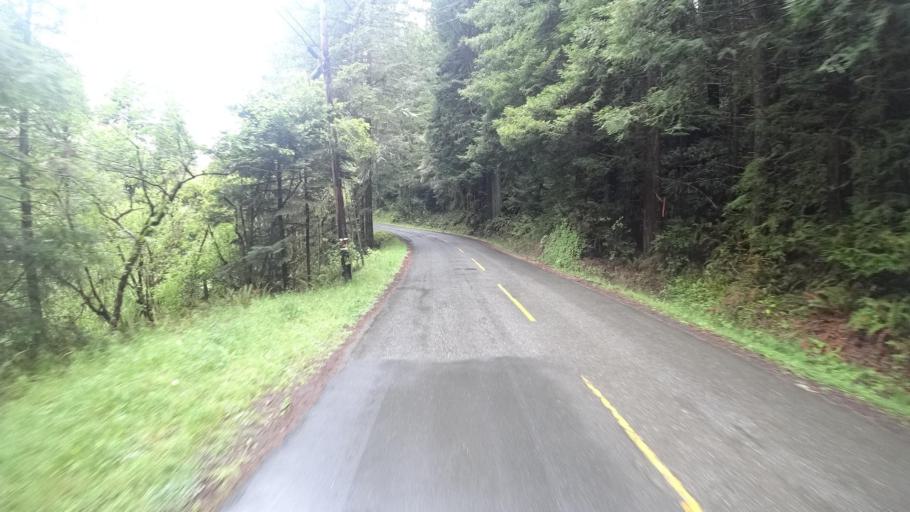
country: US
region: California
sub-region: Humboldt County
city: Bayside
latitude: 40.8172
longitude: -124.0286
